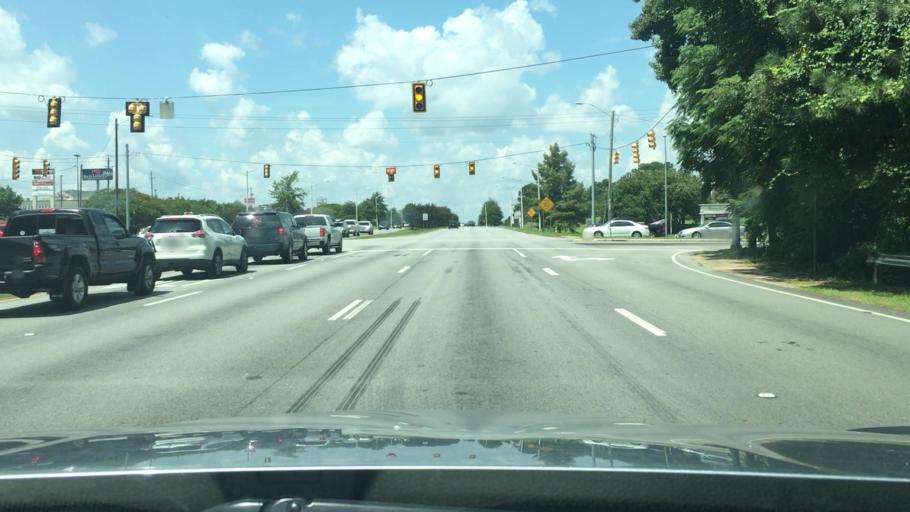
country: US
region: South Carolina
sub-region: Florence County
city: Florence
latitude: 34.1887
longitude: -79.8284
